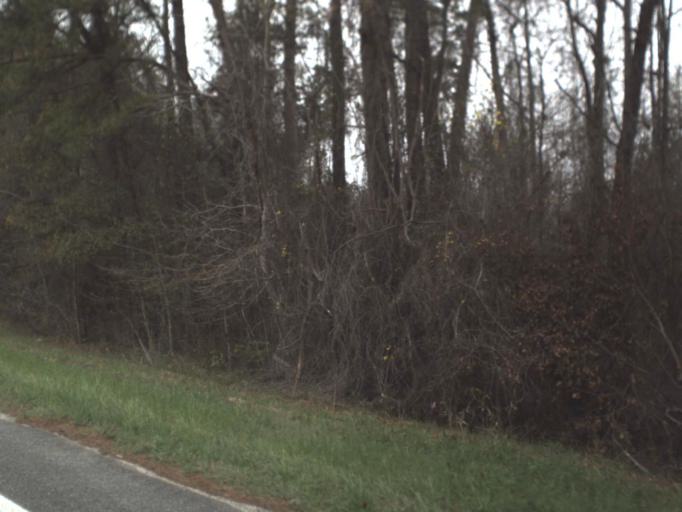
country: US
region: Florida
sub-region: Jefferson County
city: Monticello
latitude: 30.5309
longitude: -83.8156
